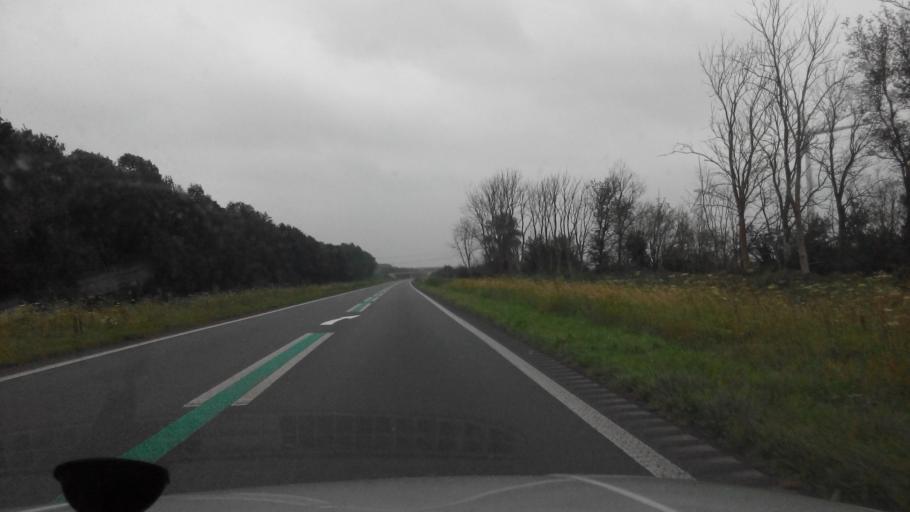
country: NL
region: Utrecht
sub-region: Gemeente Bunschoten
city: Bunschoten
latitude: 52.3164
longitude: 5.4383
